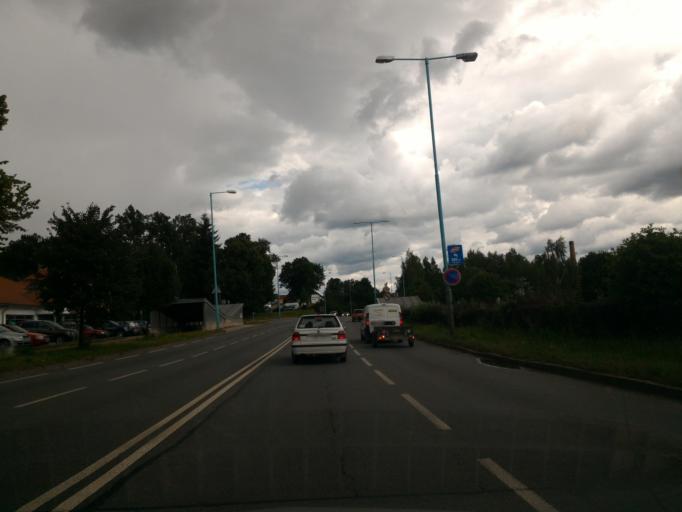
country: CZ
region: Vysocina
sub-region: Okres Pelhrimov
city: Pelhrimov
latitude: 49.4247
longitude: 15.2245
